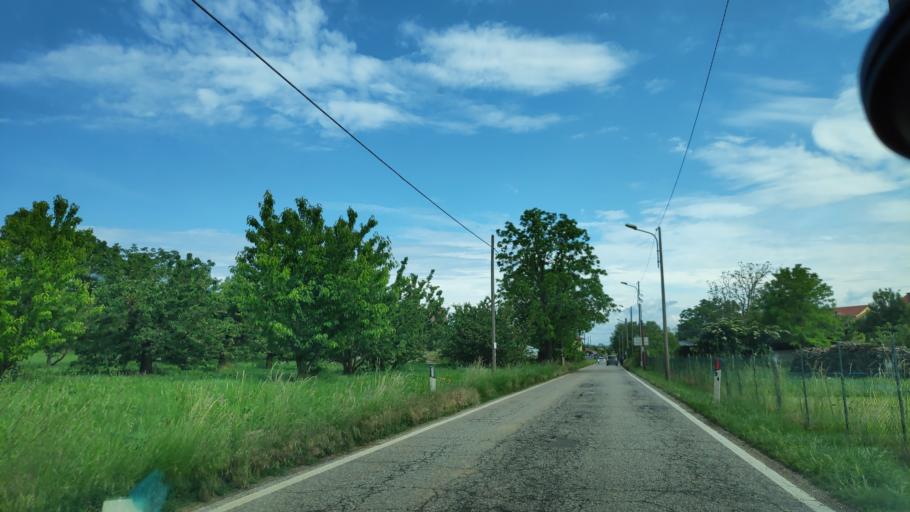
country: IT
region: Piedmont
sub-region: Provincia di Torino
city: Pecetto
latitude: 44.9995
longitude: 7.7697
